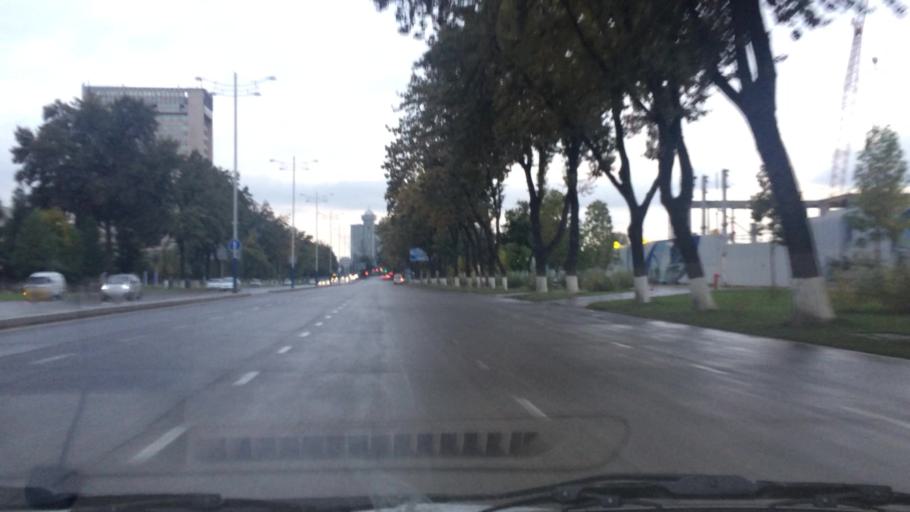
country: UZ
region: Toshkent Shahri
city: Tashkent
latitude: 41.3116
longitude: 69.2505
